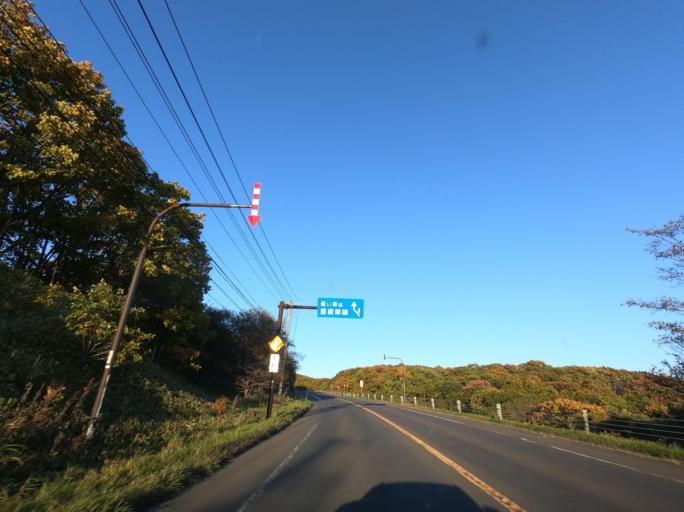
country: JP
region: Hokkaido
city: Kushiro
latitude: 43.0689
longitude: 144.3165
